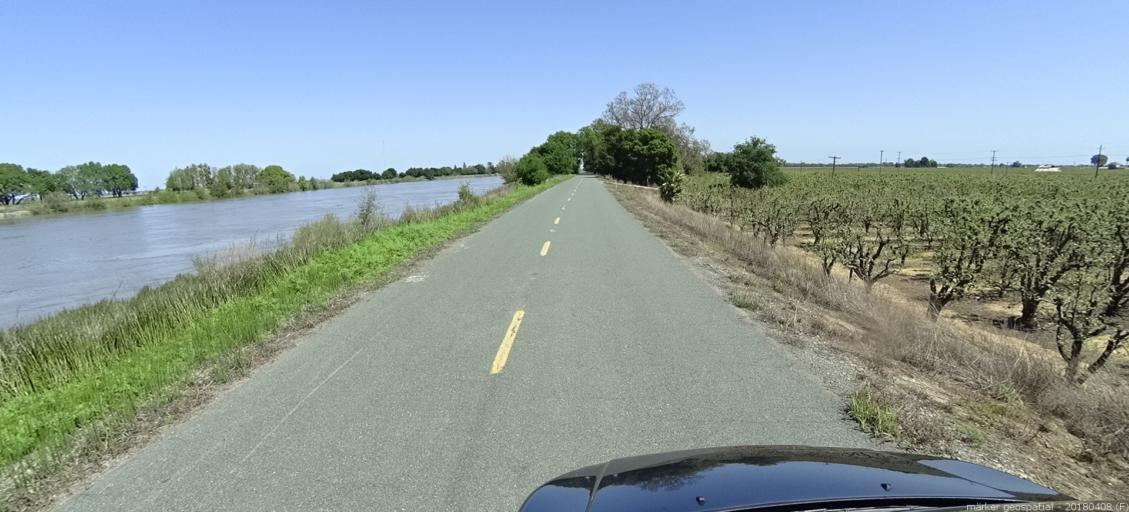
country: US
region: California
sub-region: Sacramento County
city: Walnut Grove
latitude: 38.3429
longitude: -121.5573
